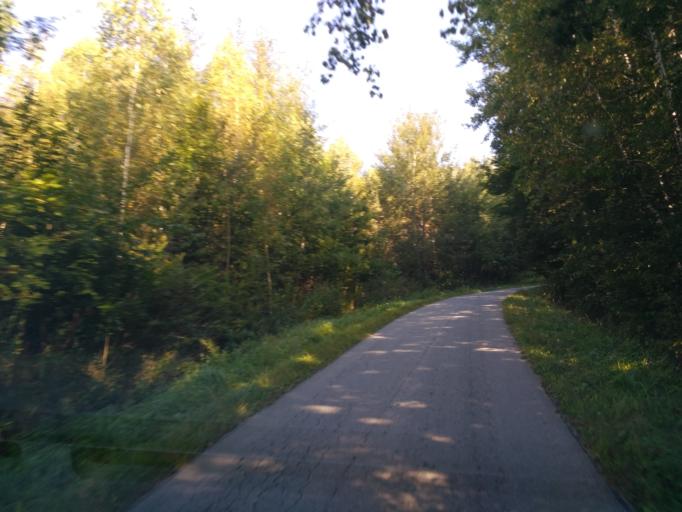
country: PL
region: Subcarpathian Voivodeship
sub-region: Powiat strzyzowski
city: Strzyzow
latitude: 49.8491
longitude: 21.8242
